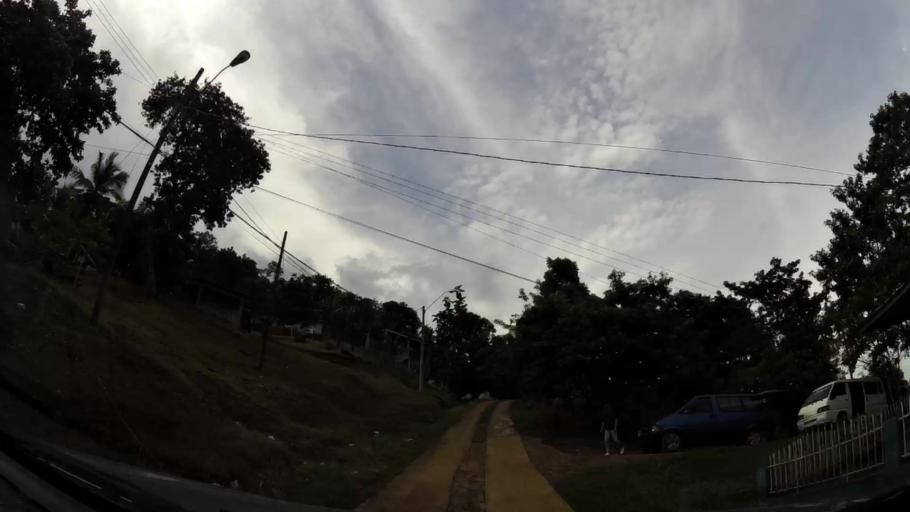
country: PA
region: Panama
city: Guadalupe
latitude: 8.8586
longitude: -79.8141
